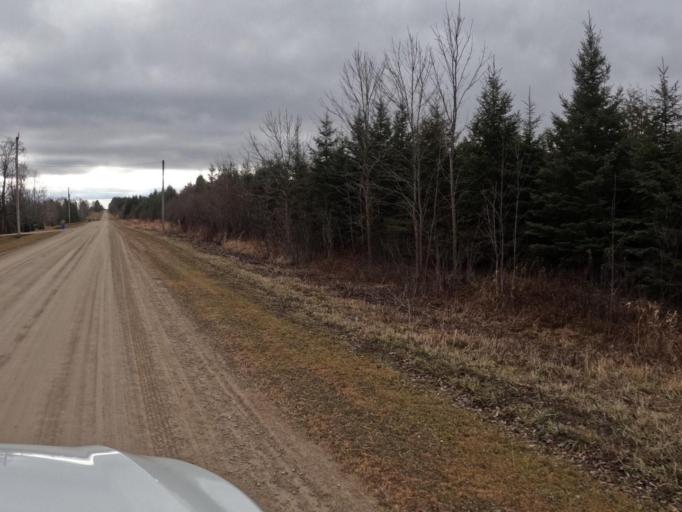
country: CA
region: Ontario
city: Shelburne
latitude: 43.9707
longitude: -80.4022
